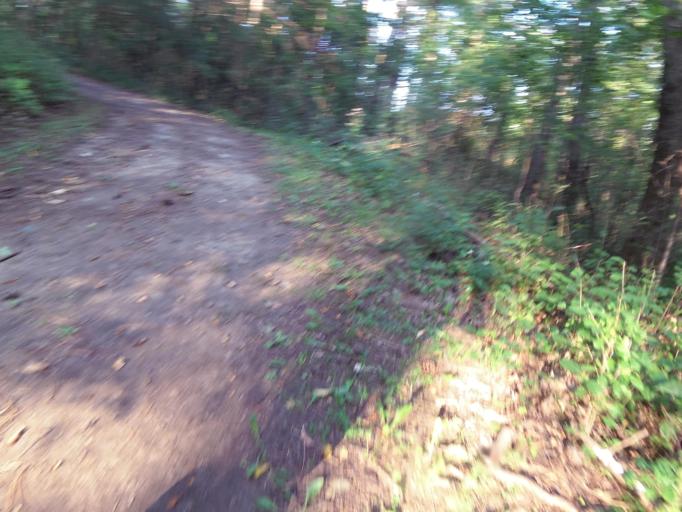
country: US
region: Minnesota
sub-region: Washington County
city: Afton
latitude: 44.8459
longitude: -92.7735
